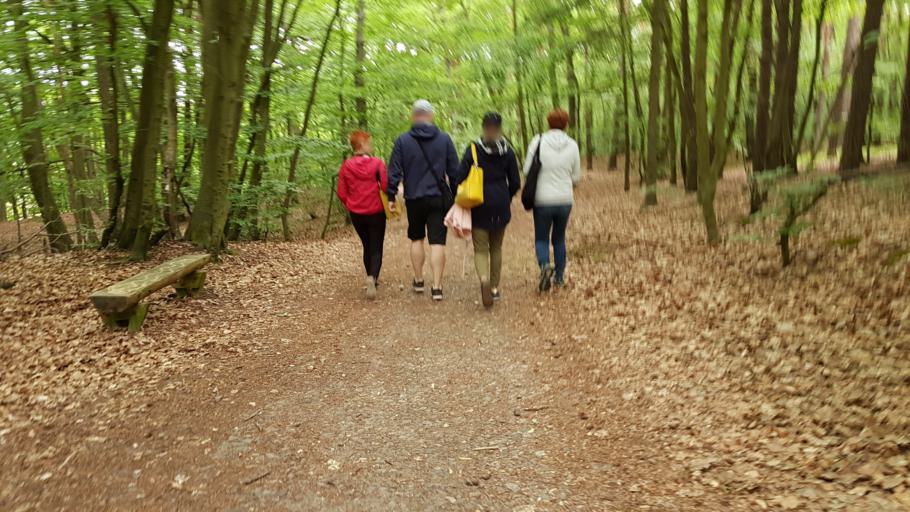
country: PL
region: West Pomeranian Voivodeship
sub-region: Powiat kamienski
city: Miedzyzdroje
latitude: 53.9333
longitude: 14.4607
